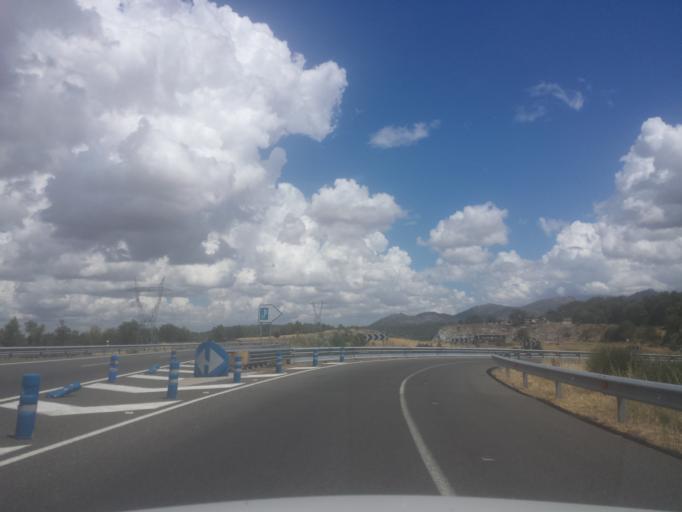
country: ES
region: Castille and Leon
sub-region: Provincia de Salamanca
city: Cantagallo
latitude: 40.3747
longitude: -5.8237
